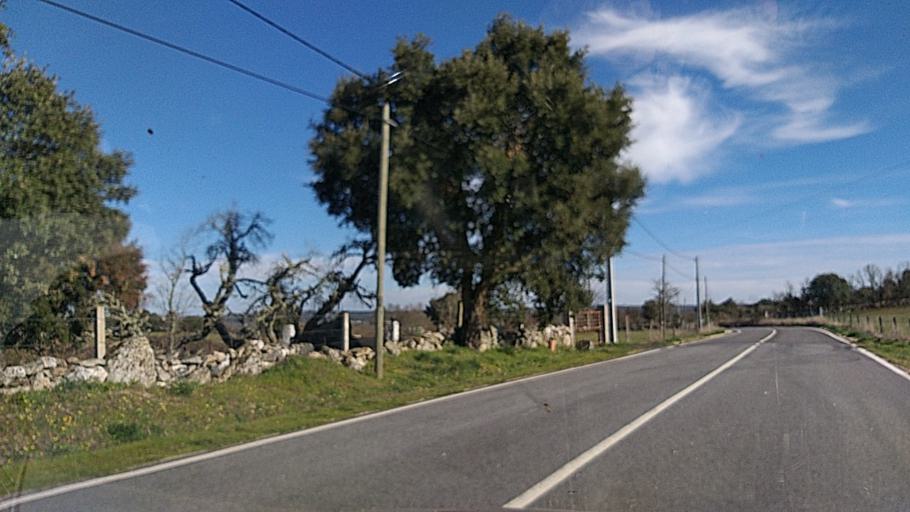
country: ES
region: Castille and Leon
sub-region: Provincia de Salamanca
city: Fuentes de Onoro
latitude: 40.6011
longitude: -6.9465
